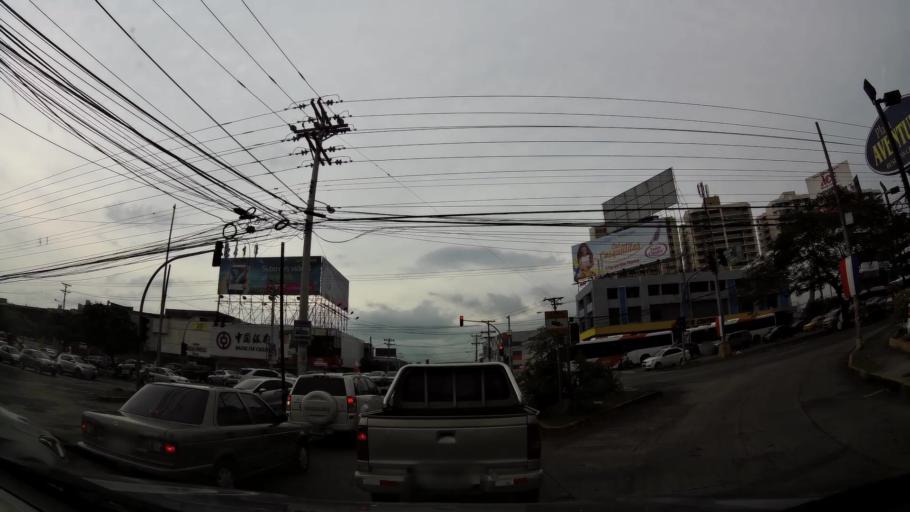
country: PA
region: Panama
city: Panama
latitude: 9.0113
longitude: -79.5344
